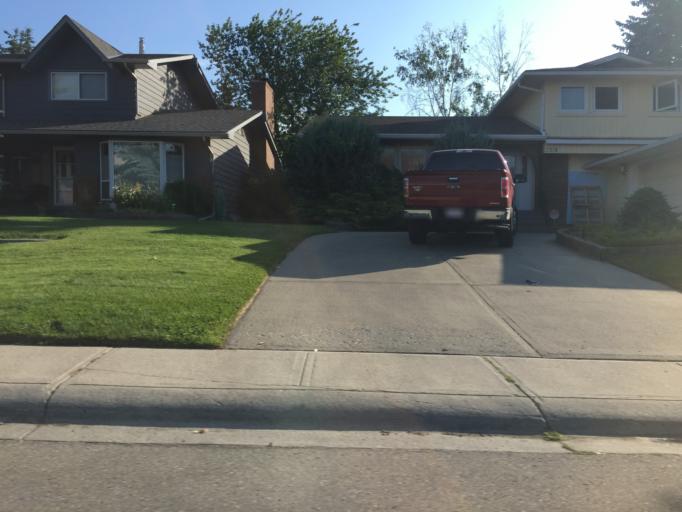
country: CA
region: Alberta
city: Calgary
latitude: 50.9409
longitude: -114.0606
